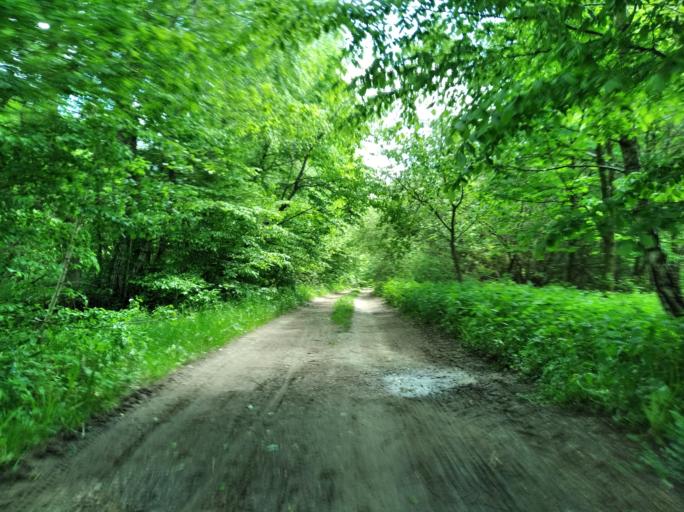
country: PL
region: Subcarpathian Voivodeship
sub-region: Powiat strzyzowski
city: Frysztak
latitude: 49.8351
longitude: 21.5592
